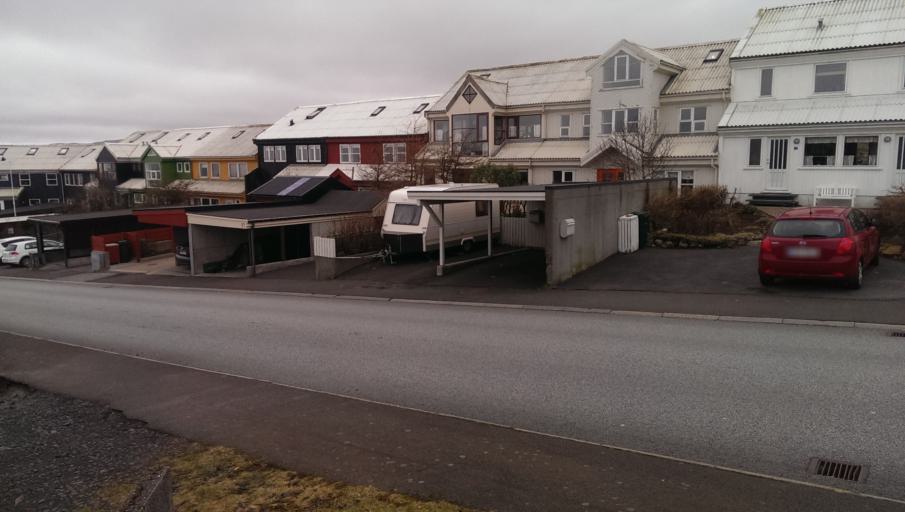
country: FO
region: Streymoy
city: Hoyvik
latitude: 62.0343
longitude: -6.7920
